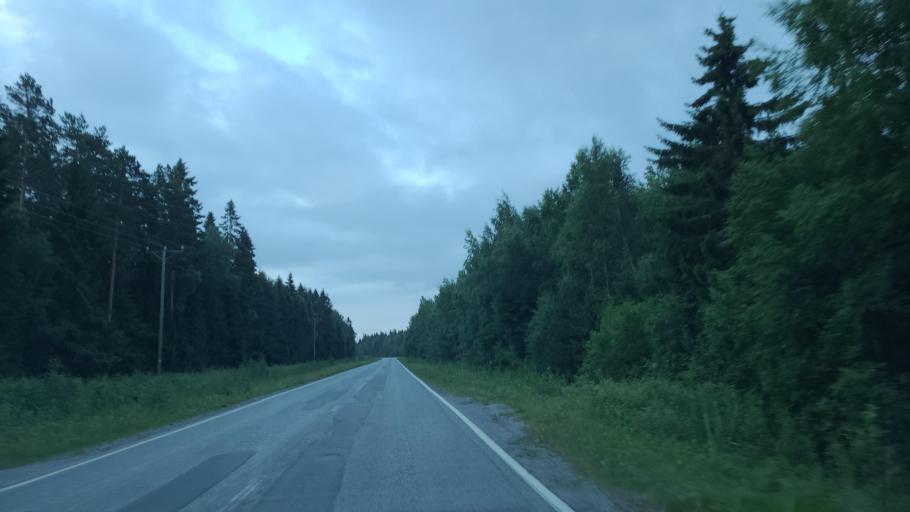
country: FI
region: Ostrobothnia
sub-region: Vaasa
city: Replot
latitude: 63.2145
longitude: 21.2505
